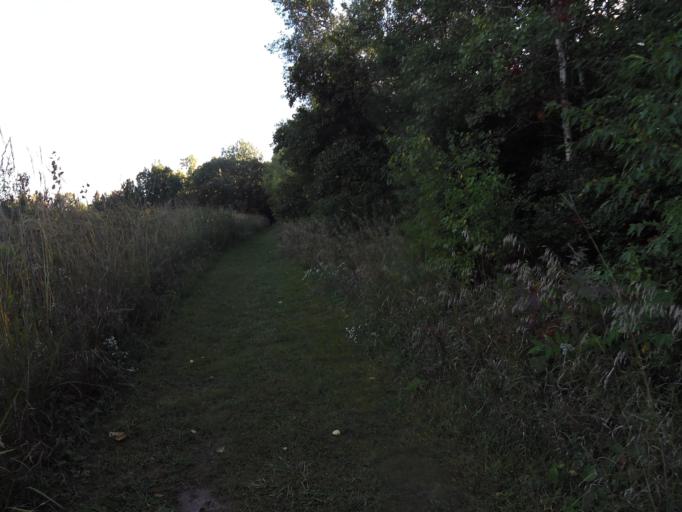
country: US
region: Minnesota
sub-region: Washington County
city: Lake Saint Croix Beach
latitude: 44.9328
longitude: -92.7918
